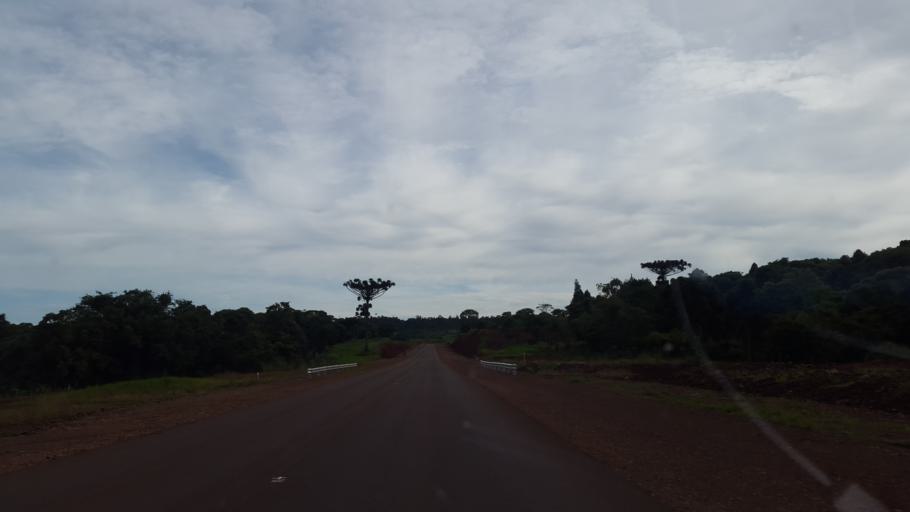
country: AR
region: Misiones
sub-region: Departamento de San Pedro
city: San Pedro
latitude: -26.4640
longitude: -53.8754
